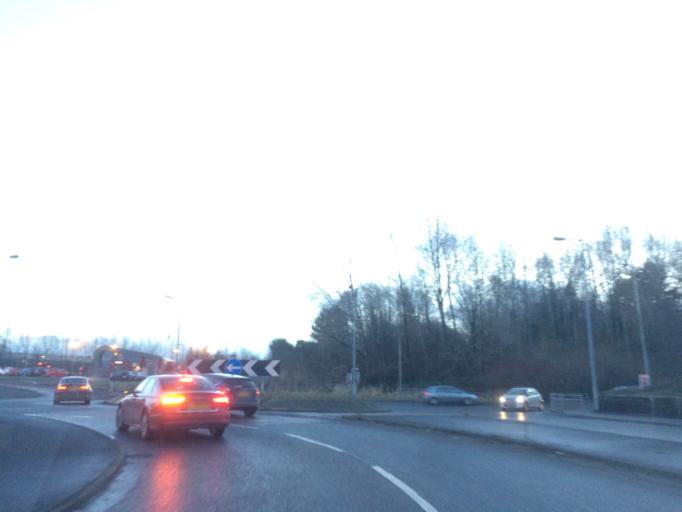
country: GB
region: Scotland
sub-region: East Renfrewshire
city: Newton Mearns
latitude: 55.8052
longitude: -4.3415
